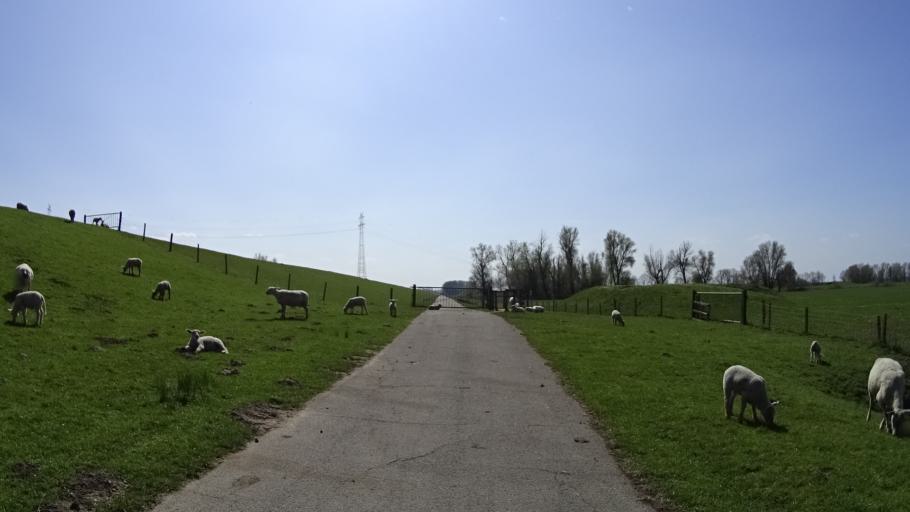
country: DE
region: Lower Saxony
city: Weener
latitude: 53.1545
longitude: 7.3715
